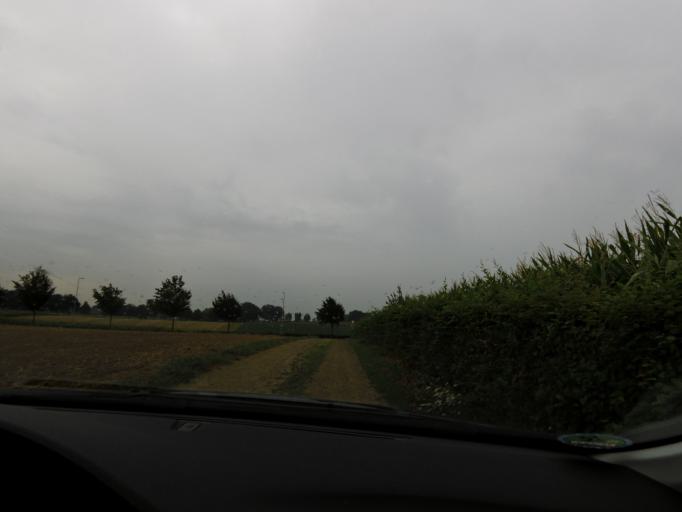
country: NL
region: Limburg
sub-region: Gemeente Simpelveld
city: Simpelveld
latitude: 50.8489
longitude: 5.9761
